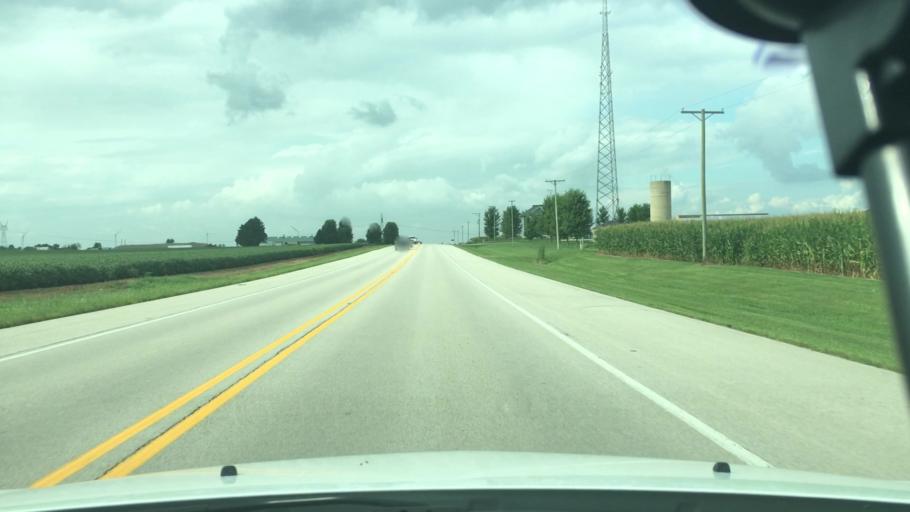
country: US
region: Illinois
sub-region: DeKalb County
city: Waterman
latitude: 41.7935
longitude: -88.7541
